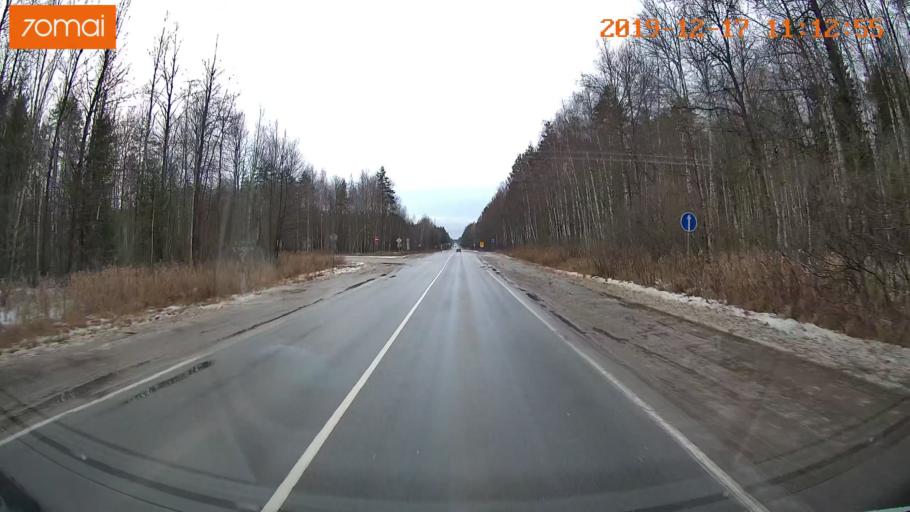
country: RU
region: Vladimir
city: Gus'-Khrustal'nyy
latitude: 55.5699
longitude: 40.6238
